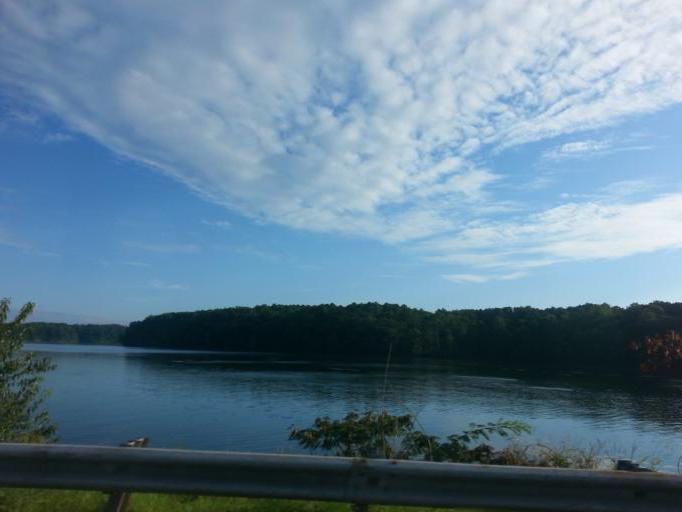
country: US
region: Alabama
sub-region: Lauderdale County
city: Rogersville
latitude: 34.8436
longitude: -87.3718
